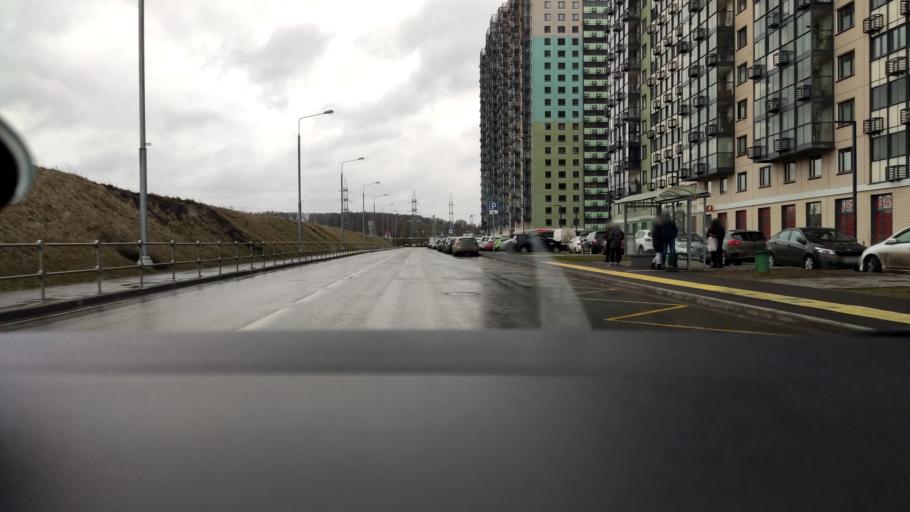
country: RU
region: Moskovskaya
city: Pavshino
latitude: 55.8613
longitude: 37.3719
